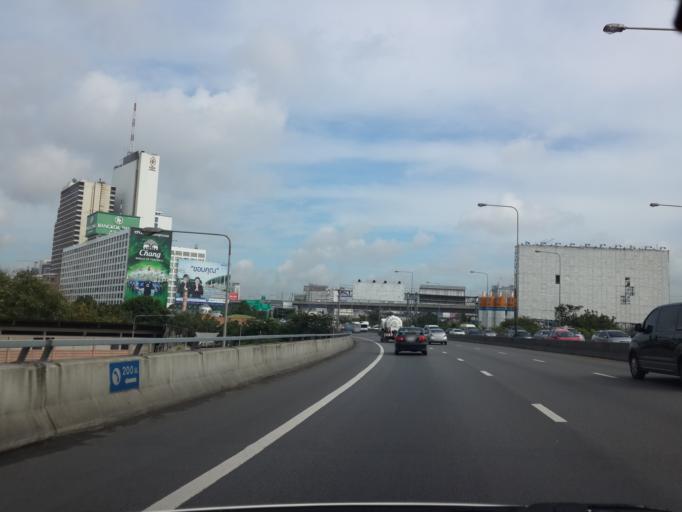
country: TH
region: Bangkok
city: Ratchathewi
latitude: 13.7507
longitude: 100.5493
